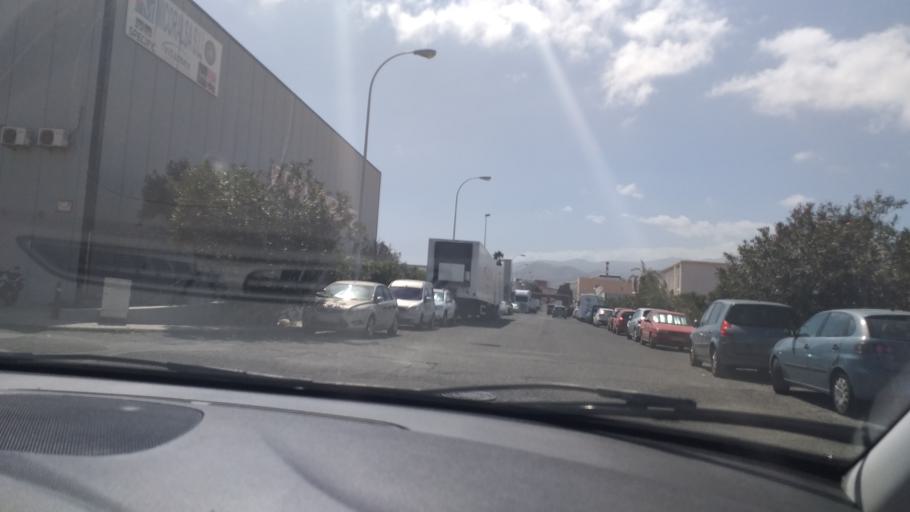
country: ES
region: Canary Islands
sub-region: Provincia de Las Palmas
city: Telde
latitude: 27.9803
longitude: -15.3787
